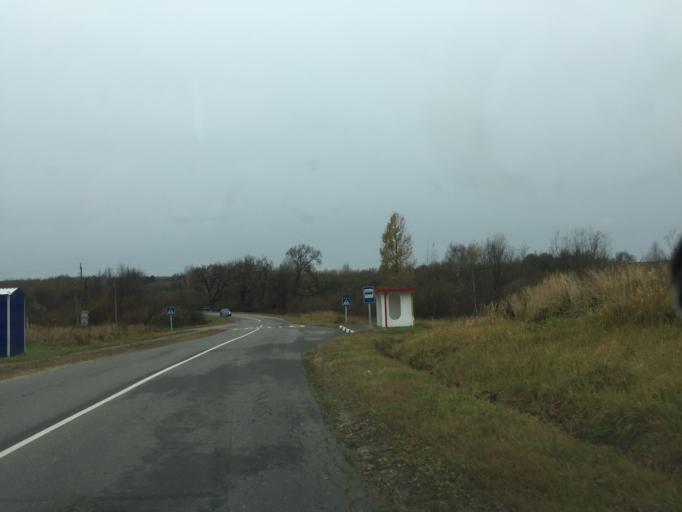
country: BY
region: Mogilev
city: Chavusy
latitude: 53.9023
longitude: 31.0551
